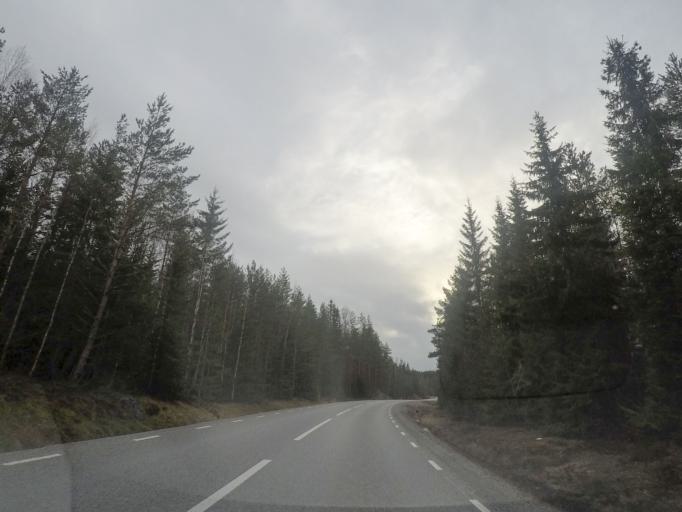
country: SE
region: OErebro
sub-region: Lindesbergs Kommun
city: Stora
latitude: 59.8929
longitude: 15.1790
